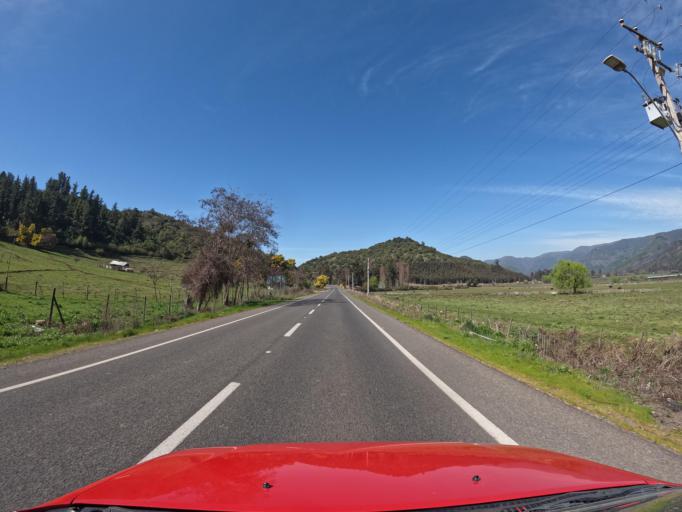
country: CL
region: Maule
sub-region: Provincia de Curico
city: Teno
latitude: -34.9782
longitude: -70.9726
